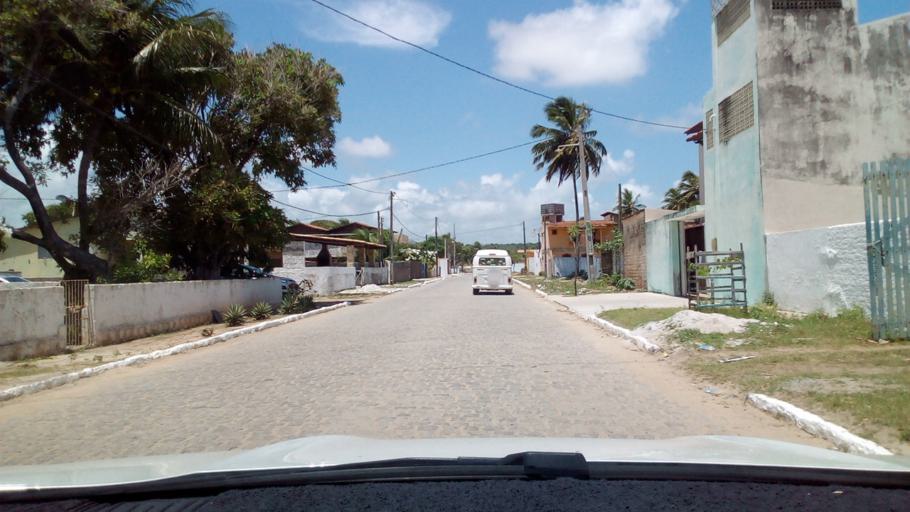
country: BR
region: Paraiba
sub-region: Pitimbu
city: Pitimbu
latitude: -7.5009
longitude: -34.8134
